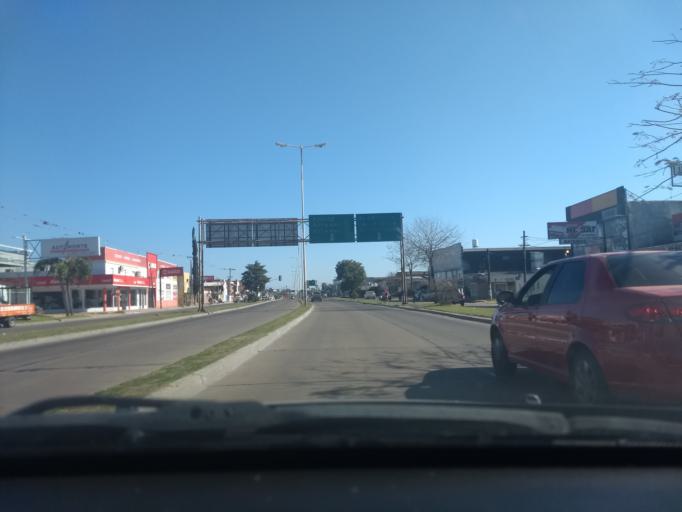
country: AR
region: Corrientes
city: Corrientes
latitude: -27.4797
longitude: -58.8048
